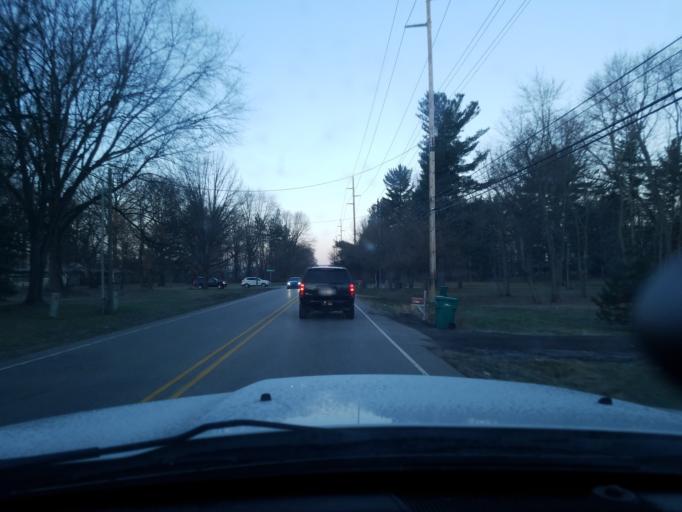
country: US
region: Indiana
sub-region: Marion County
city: Meridian Hills
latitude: 39.8971
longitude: -86.2194
